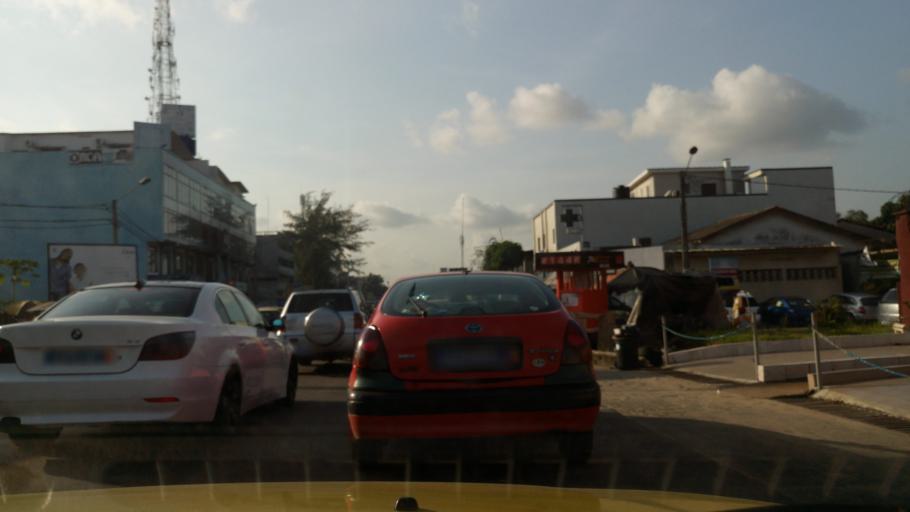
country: CI
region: Lagunes
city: Abobo
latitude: 5.4006
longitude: -3.9781
